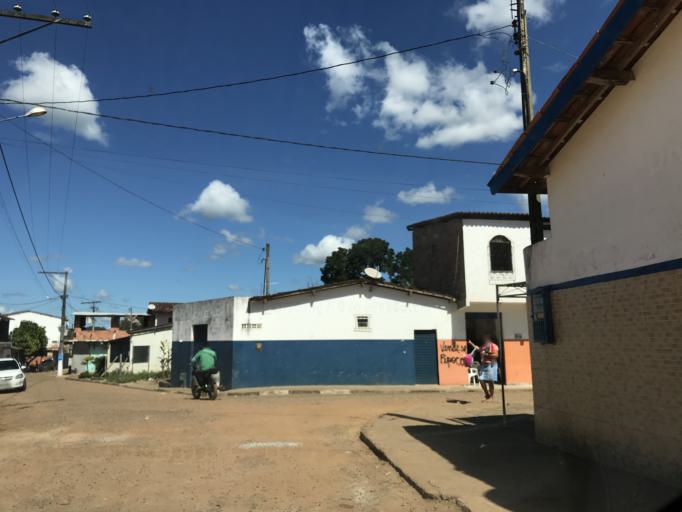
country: BR
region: Bahia
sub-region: Valenca
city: Valenca
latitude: -13.3237
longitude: -39.2415
